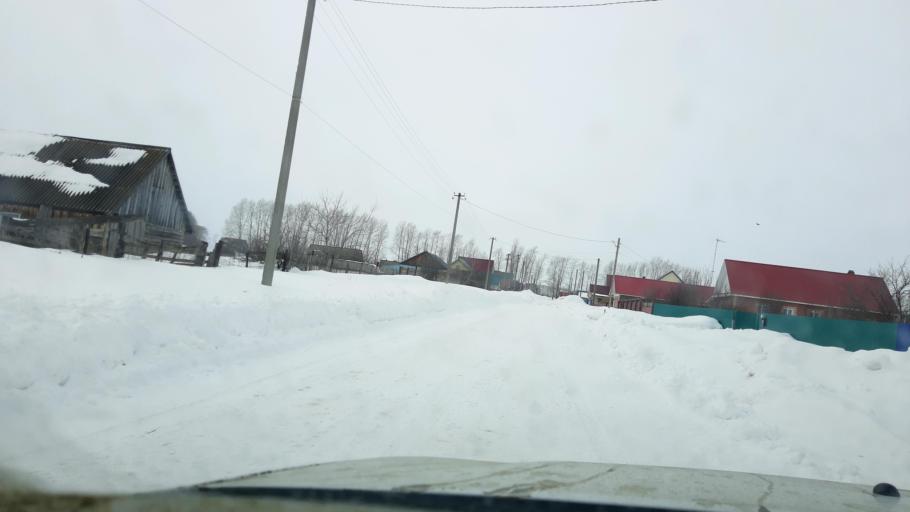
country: RU
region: Bashkortostan
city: Karmaskaly
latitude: 54.4205
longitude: 56.1673
